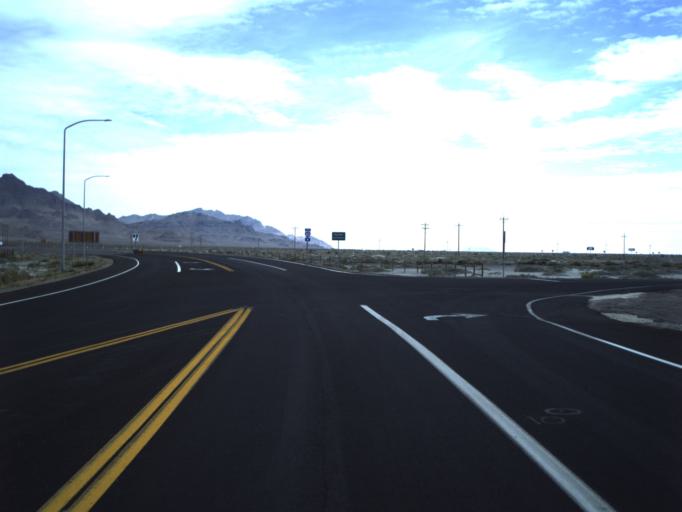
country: US
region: Utah
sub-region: Tooele County
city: Wendover
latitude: 40.7393
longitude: -114.0205
